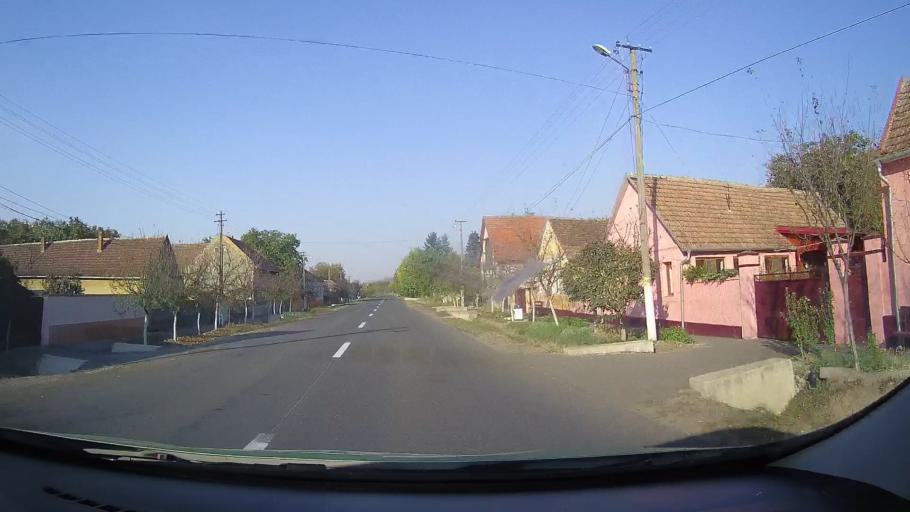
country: RO
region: Arad
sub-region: Comuna Ghioroc
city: Cuvin
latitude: 46.1700
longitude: 21.5955
